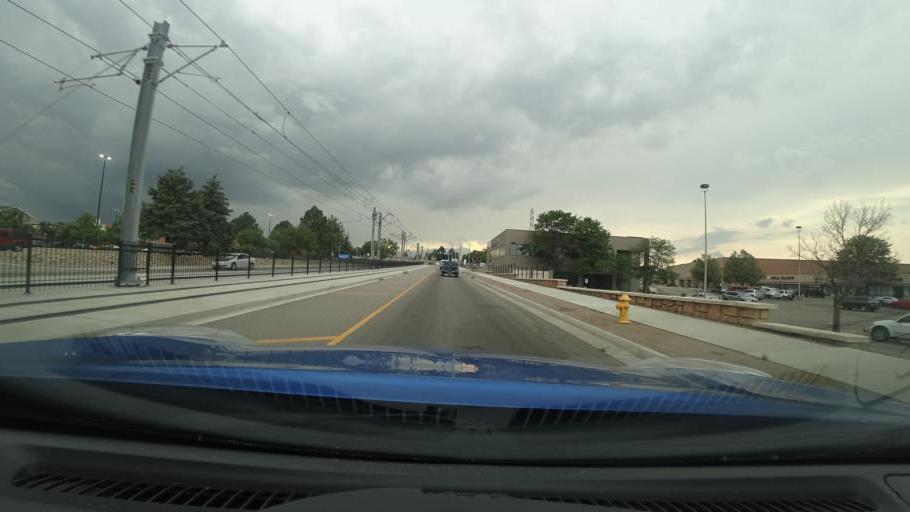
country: US
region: Colorado
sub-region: Adams County
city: Aurora
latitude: 39.7040
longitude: -104.8258
